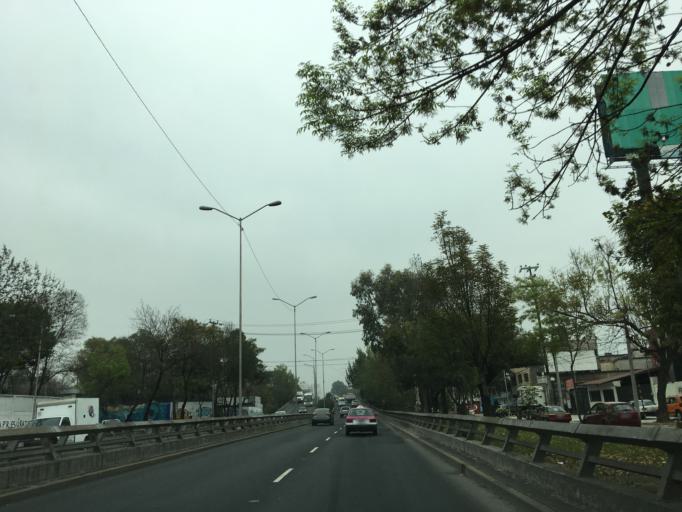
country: MX
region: Mexico City
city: Tlalpan
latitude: 19.3058
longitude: -99.1426
